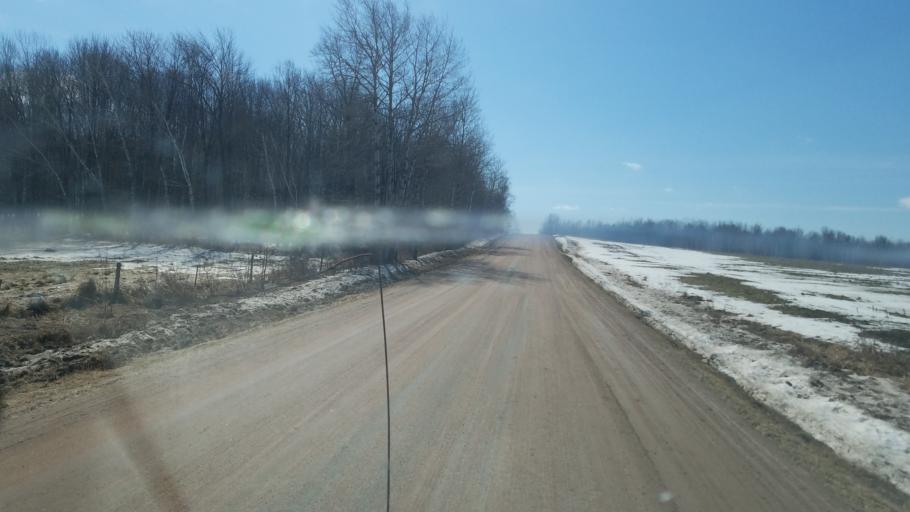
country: US
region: Wisconsin
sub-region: Clark County
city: Loyal
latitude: 44.6114
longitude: -90.3970
